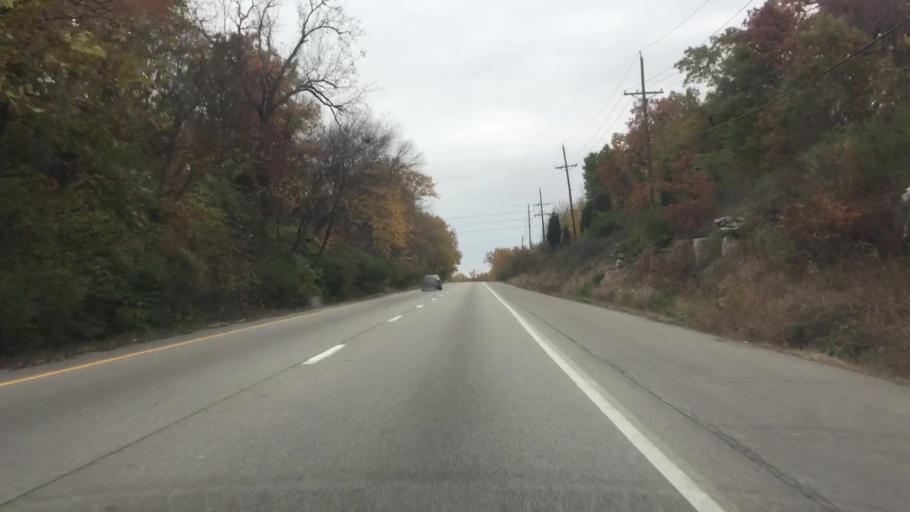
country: US
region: Missouri
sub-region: Jackson County
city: Raytown
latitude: 38.9696
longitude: -94.4369
